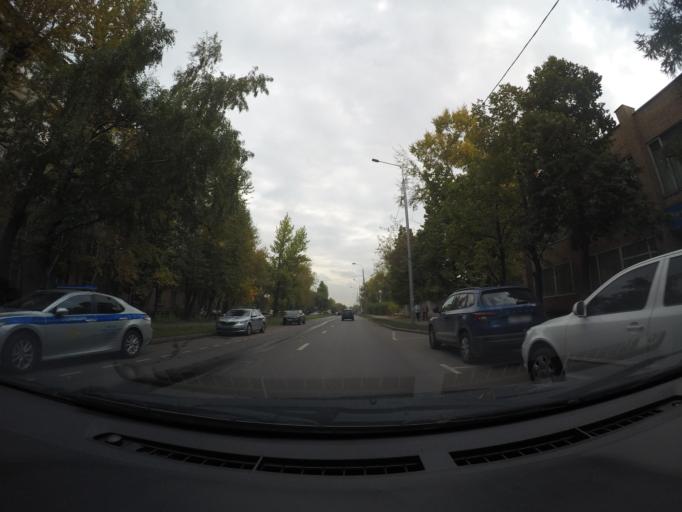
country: RU
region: Moscow
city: Lefortovo
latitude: 55.7611
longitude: 37.7310
